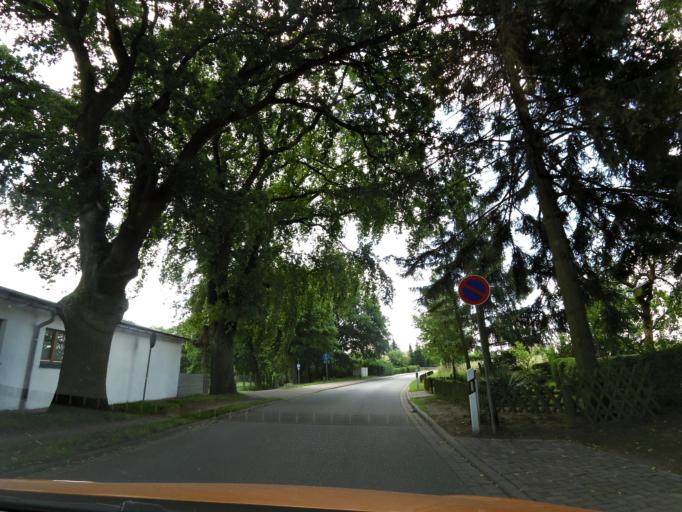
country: DE
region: Mecklenburg-Vorpommern
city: Plau am See
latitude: 53.4479
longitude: 12.2817
